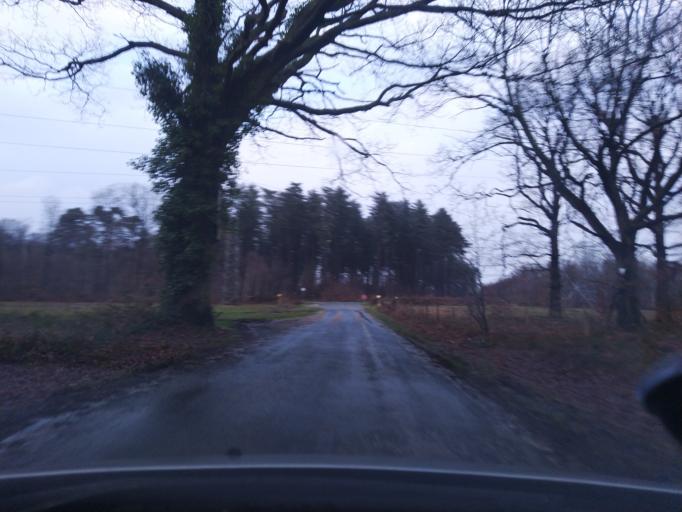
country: FR
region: Haute-Normandie
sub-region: Departement de la Seine-Maritime
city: Saint-Pierre-de-Varengeville
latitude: 49.4948
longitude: 0.9077
